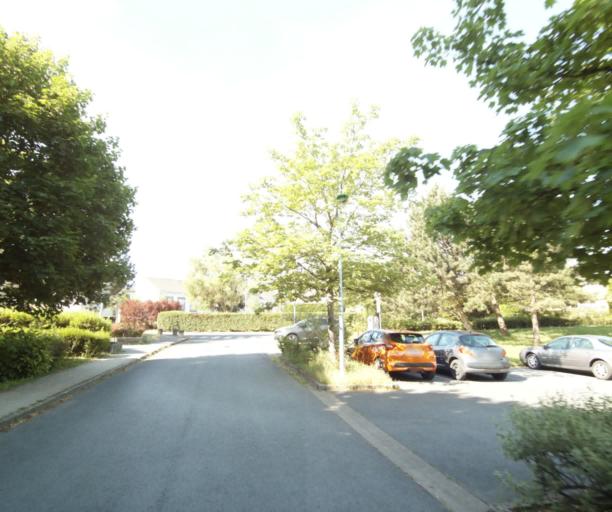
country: FR
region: Champagne-Ardenne
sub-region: Departement des Ardennes
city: La Francheville
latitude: 49.7401
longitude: 4.7181
